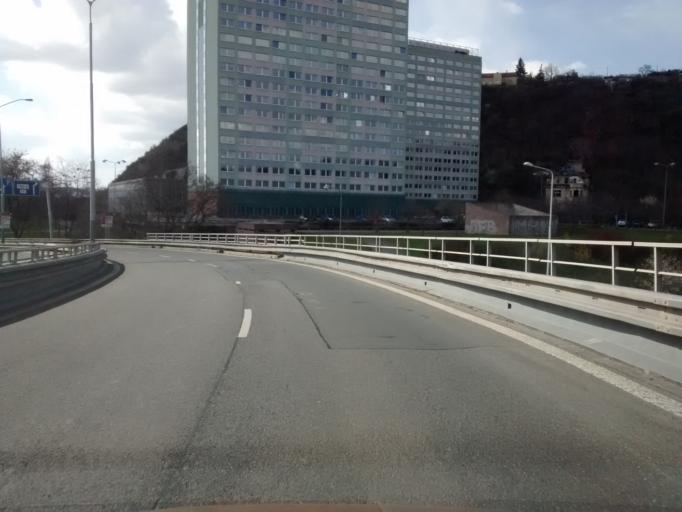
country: CZ
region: Praha
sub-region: Praha 8
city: Karlin
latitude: 50.1157
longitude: 14.4450
